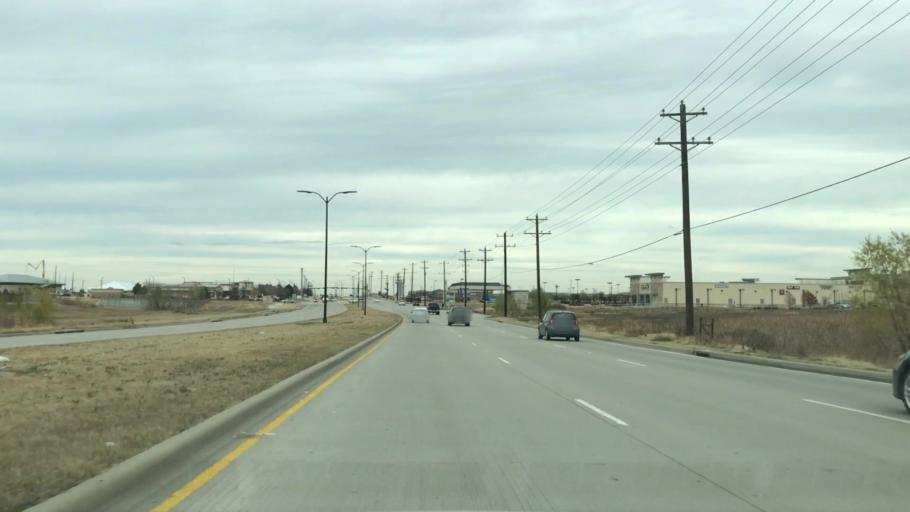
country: US
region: Texas
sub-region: Denton County
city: The Colony
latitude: 33.1222
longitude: -96.8914
